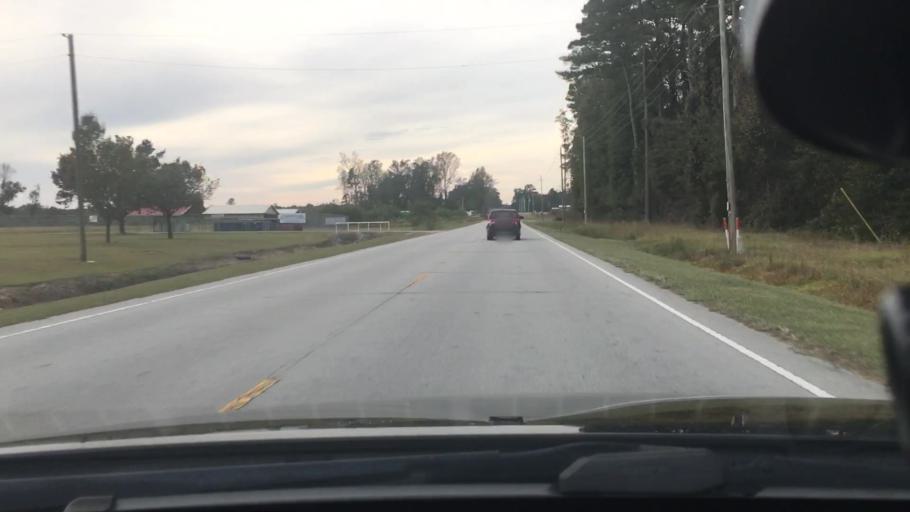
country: US
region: North Carolina
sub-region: Pitt County
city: Windsor
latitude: 35.4715
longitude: -77.2856
